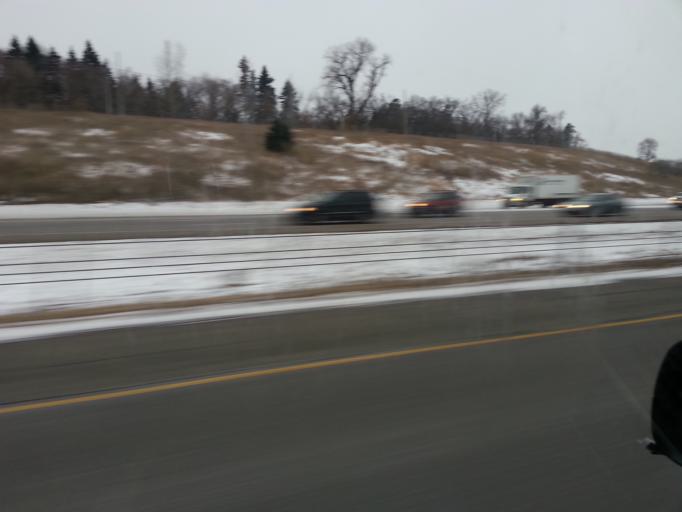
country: US
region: Minnesota
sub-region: Dakota County
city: Mendota Heights
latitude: 44.8627
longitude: -93.1213
